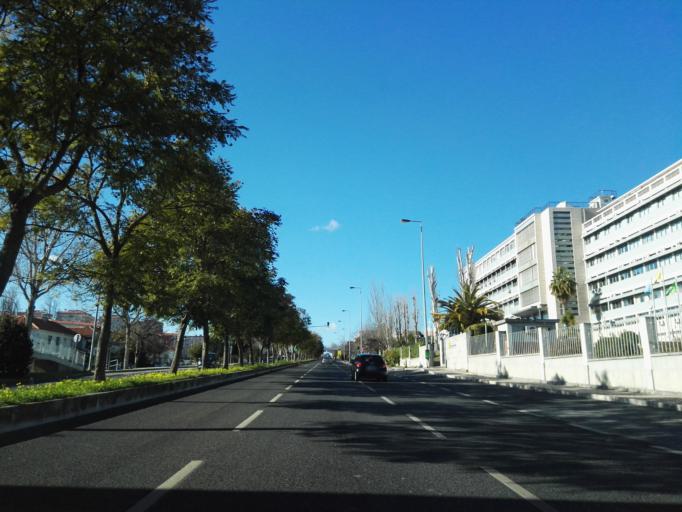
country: PT
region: Lisbon
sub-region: Loures
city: Moscavide
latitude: 38.7774
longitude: -9.1131
